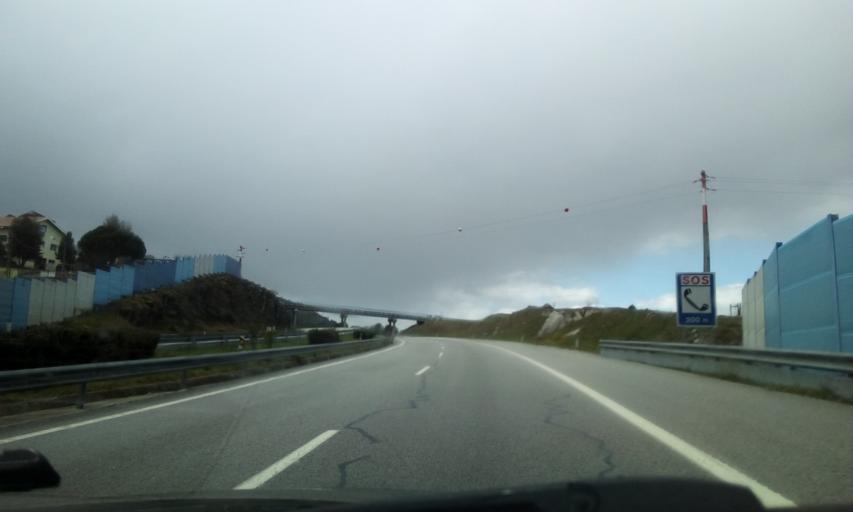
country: PT
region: Viseu
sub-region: Mangualde
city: Mangualde
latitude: 40.6160
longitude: -7.7185
